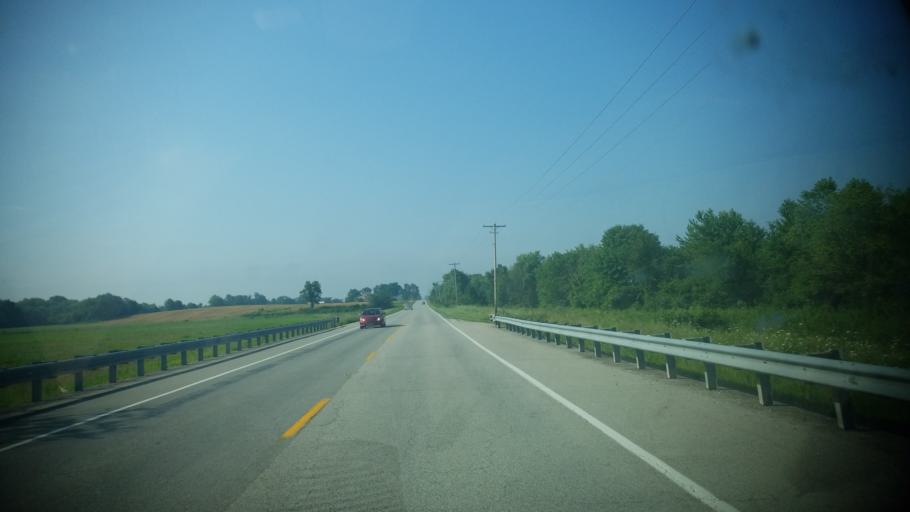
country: US
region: Illinois
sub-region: Clay County
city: Flora
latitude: 38.5954
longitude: -88.4386
